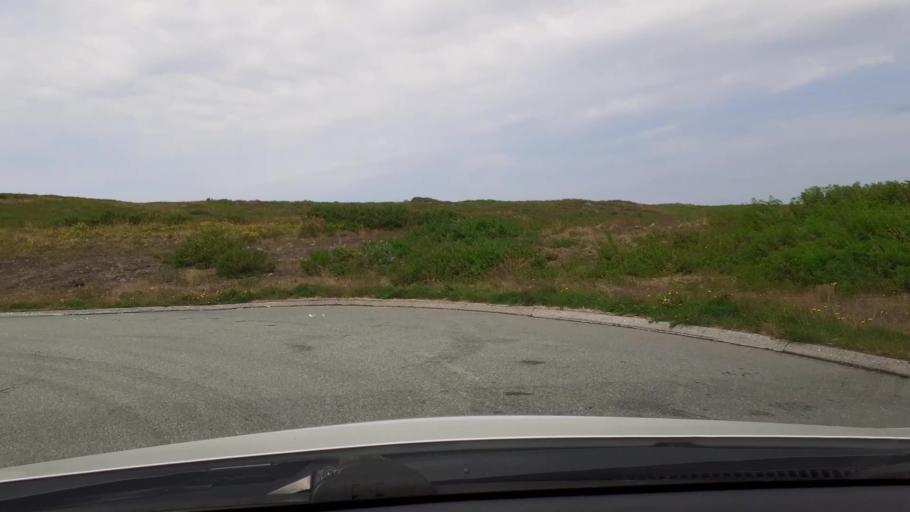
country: IS
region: Southern Peninsula
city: Vogar
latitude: 63.9637
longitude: -22.4202
